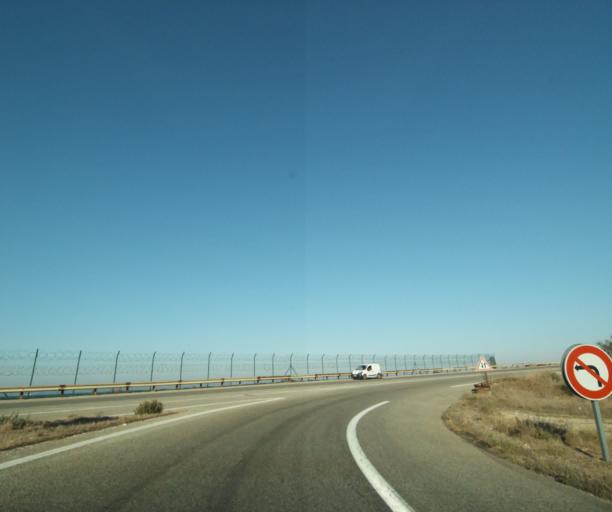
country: FR
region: Provence-Alpes-Cote d'Azur
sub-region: Departement des Bouches-du-Rhone
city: Martigues
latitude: 43.4012
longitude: 5.1016
